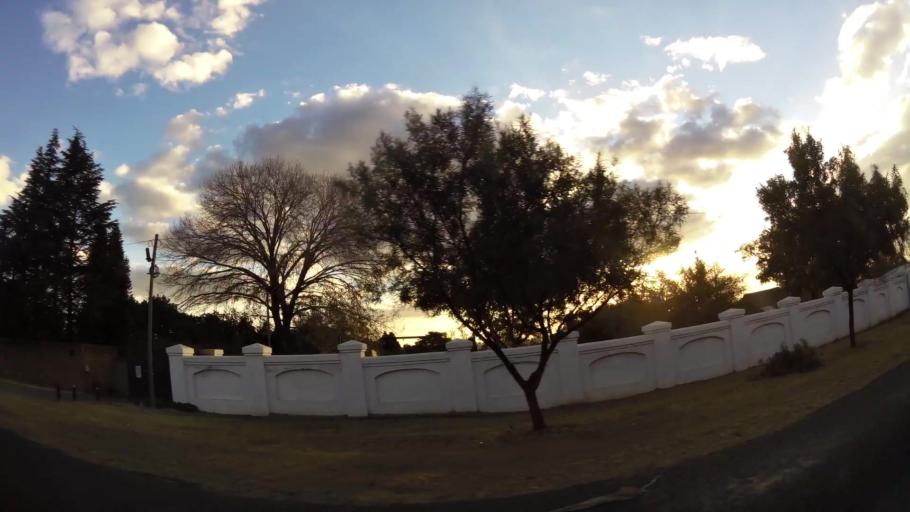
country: ZA
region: Gauteng
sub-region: City of Johannesburg Metropolitan Municipality
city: Midrand
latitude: -25.9790
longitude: 28.1531
